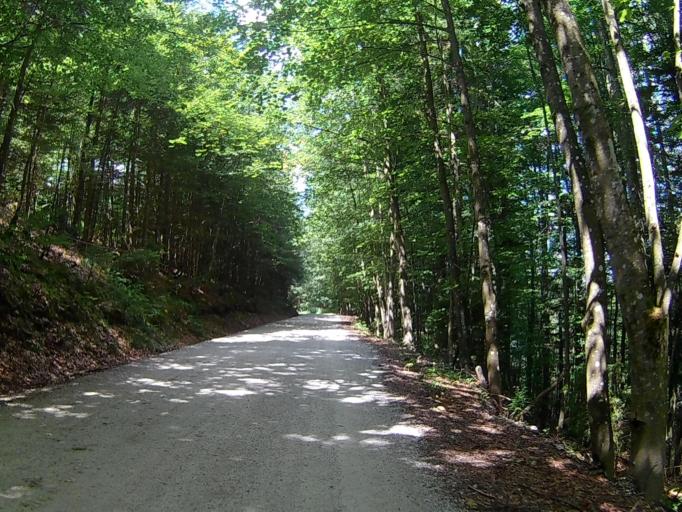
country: SI
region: Selnica ob Dravi
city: Selnica ob Dravi
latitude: 46.4836
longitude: 15.4569
